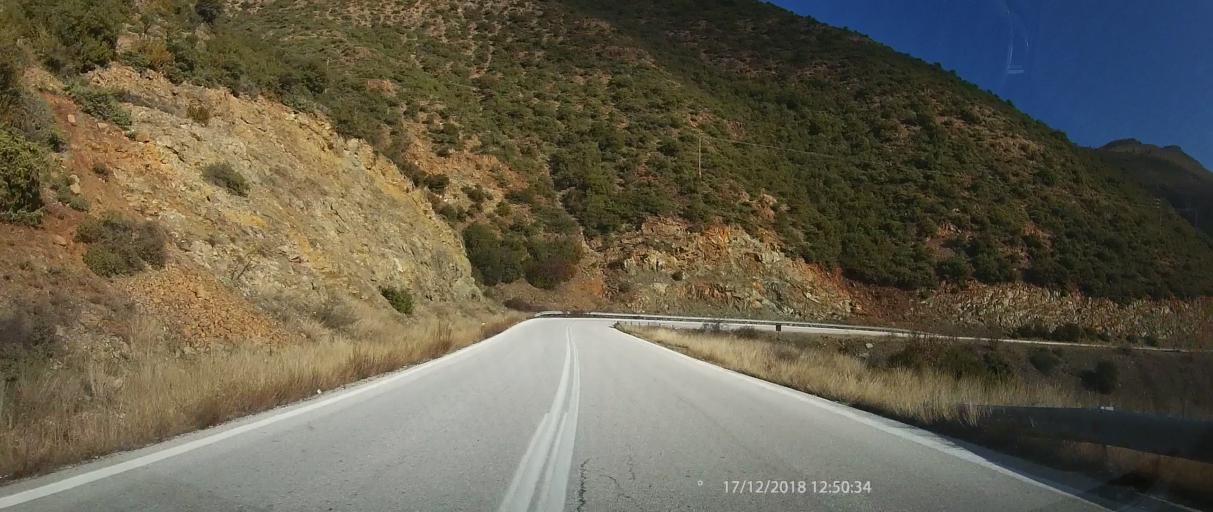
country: GR
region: Thessaly
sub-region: Trikala
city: Kastraki
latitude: 39.7718
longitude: 21.4543
